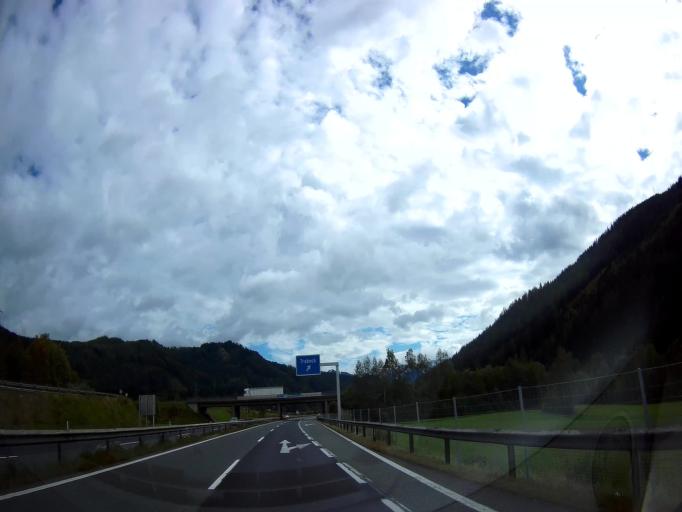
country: AT
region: Styria
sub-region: Politischer Bezirk Leoben
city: Traboch
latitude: 47.3706
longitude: 14.9900
